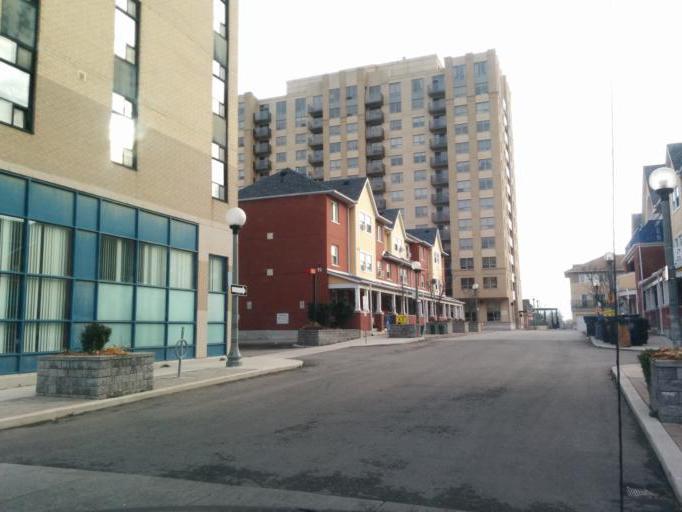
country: CA
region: Ontario
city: Etobicoke
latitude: 43.6022
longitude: -79.5108
